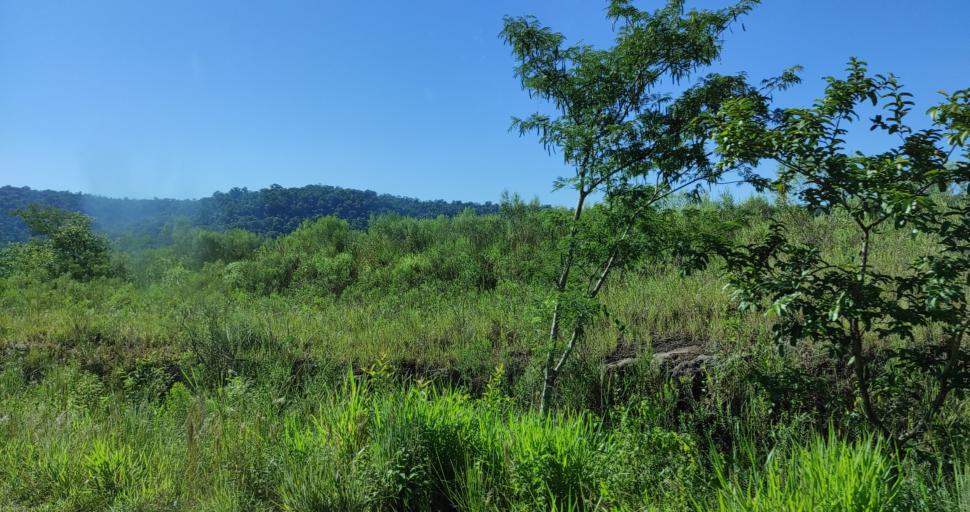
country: AR
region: Misiones
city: El Soberbio
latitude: -27.2467
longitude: -54.0285
